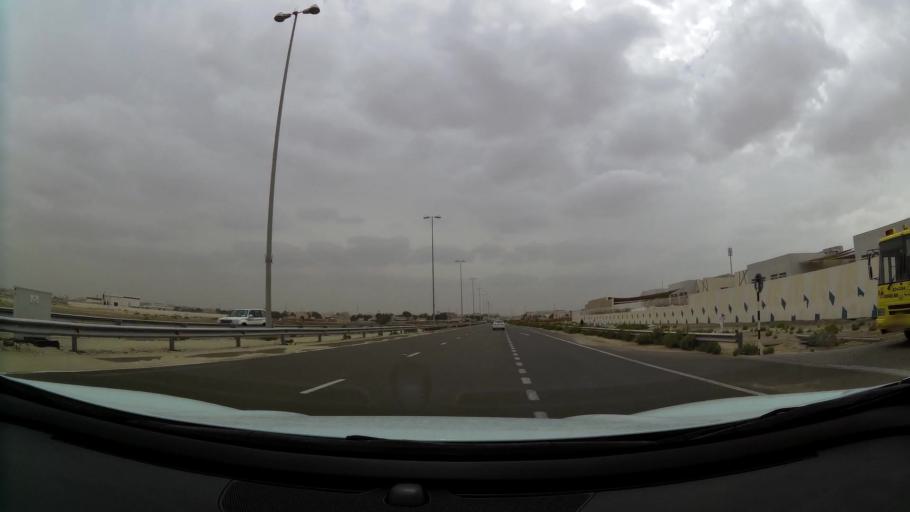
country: AE
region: Abu Dhabi
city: Abu Dhabi
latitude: 24.3265
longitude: 54.6449
